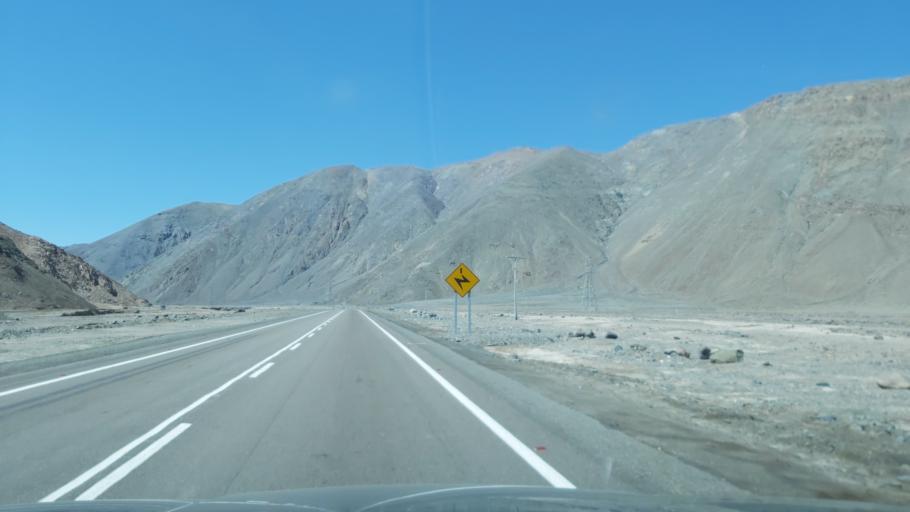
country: CL
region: Atacama
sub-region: Provincia de Chanaral
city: Diego de Almagro
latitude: -26.3412
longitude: -69.7454
